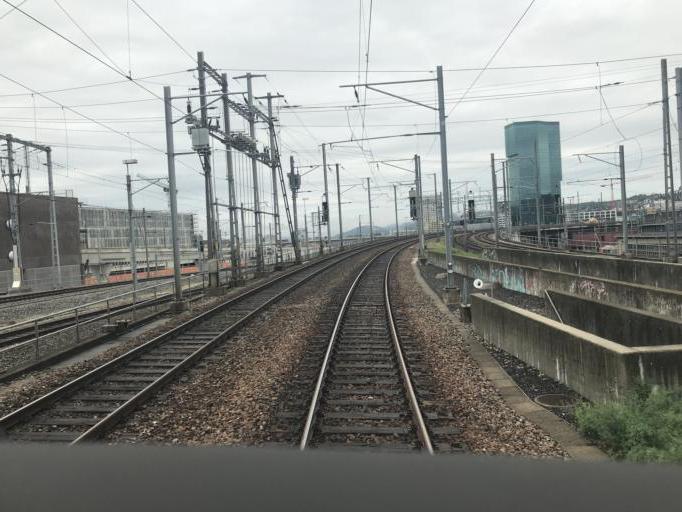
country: CH
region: Zurich
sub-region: Bezirk Zuerich
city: Aussersihl
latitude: 47.3815
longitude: 8.5230
